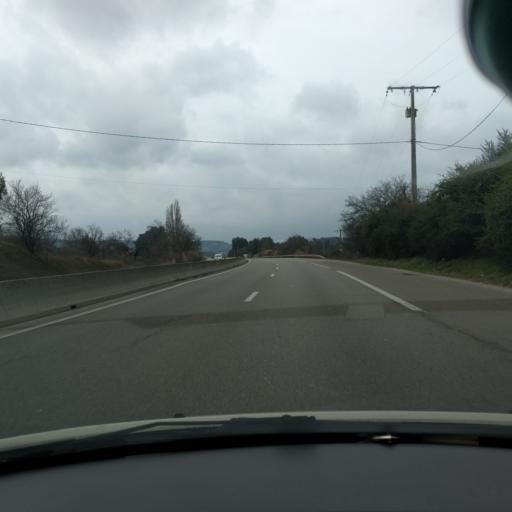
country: FR
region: Provence-Alpes-Cote d'Azur
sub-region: Departement des Bouches-du-Rhone
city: Simiane-Collongue
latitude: 43.4467
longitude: 5.4420
